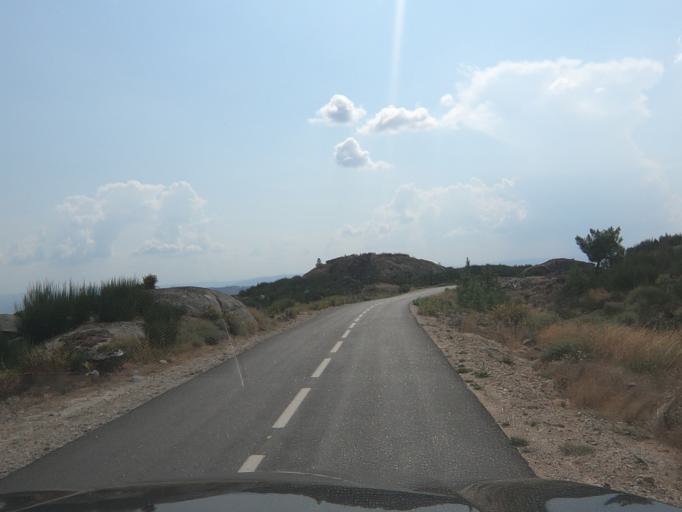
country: PT
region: Vila Real
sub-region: Sabrosa
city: Sabrosa
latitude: 41.2882
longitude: -7.6132
